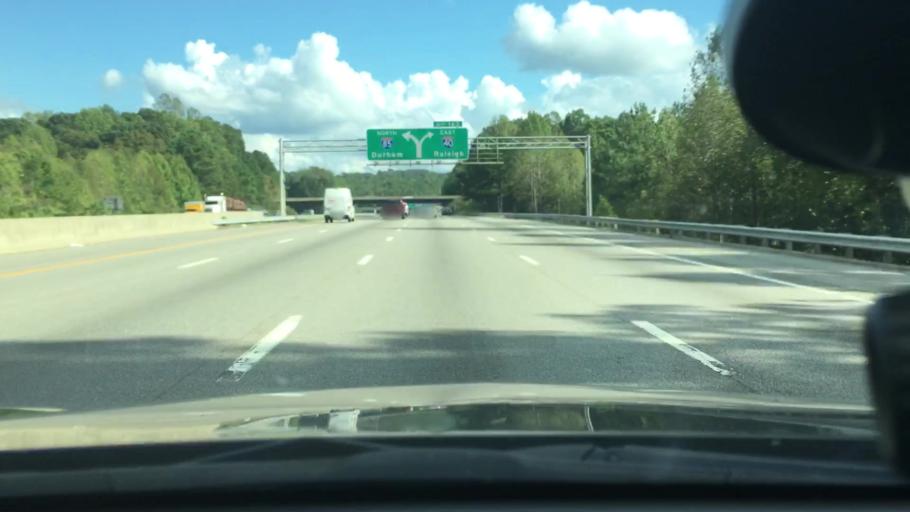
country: US
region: North Carolina
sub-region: Orange County
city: Hillsborough
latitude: 36.0630
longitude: -79.1383
